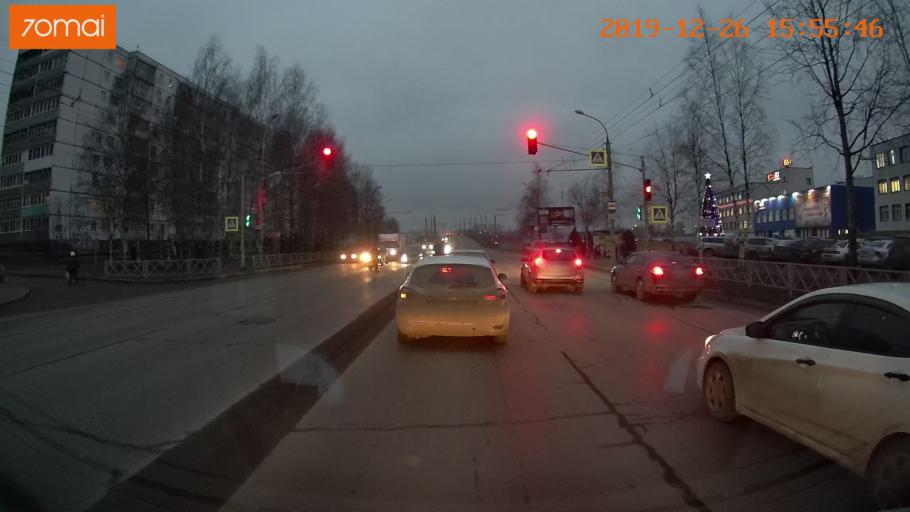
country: RU
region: Jaroslavl
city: Rybinsk
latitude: 58.0432
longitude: 38.8077
